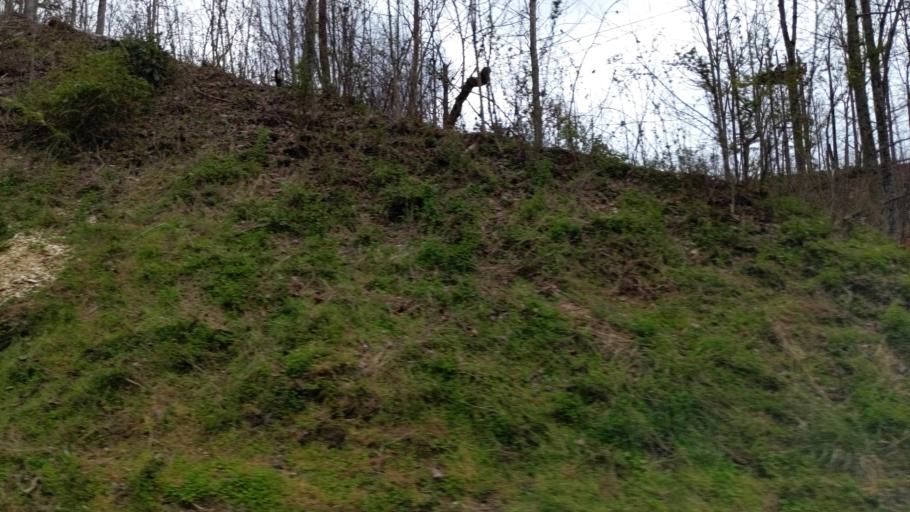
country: US
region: Tennessee
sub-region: Sevier County
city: Gatlinburg
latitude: 35.7121
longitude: -83.5093
